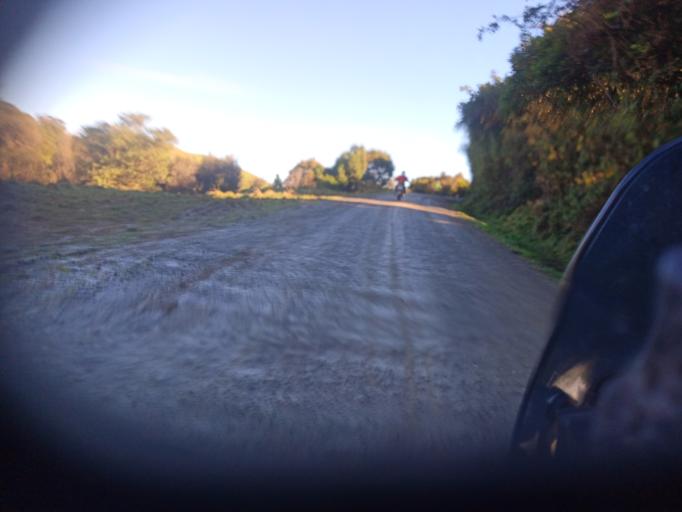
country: NZ
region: Gisborne
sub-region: Gisborne District
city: Gisborne
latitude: -38.1970
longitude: 178.0819
